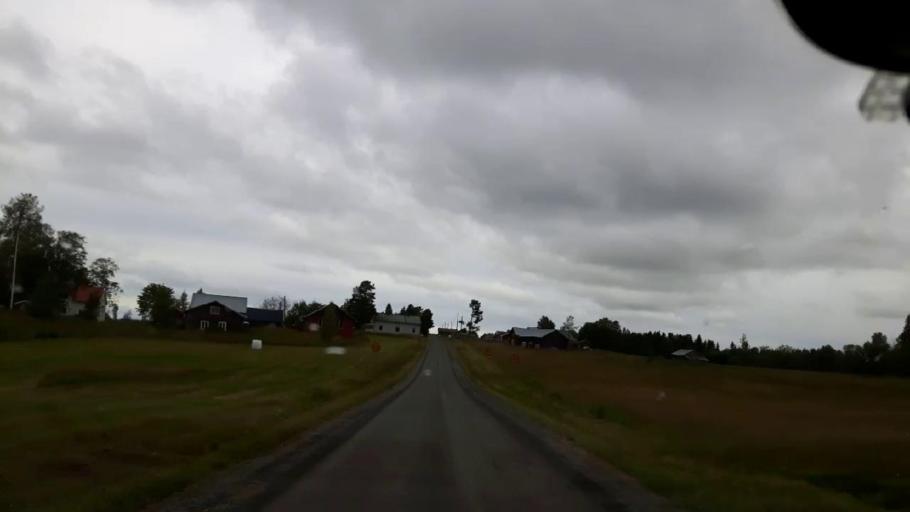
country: SE
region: Jaemtland
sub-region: OEstersunds Kommun
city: Ostersund
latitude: 63.0511
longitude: 14.5686
